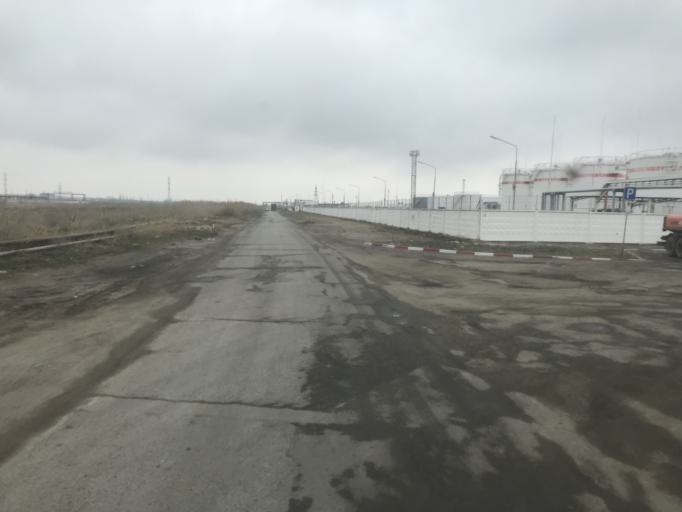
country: RU
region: Volgograd
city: Svetlyy Yar
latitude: 48.5102
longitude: 44.6393
